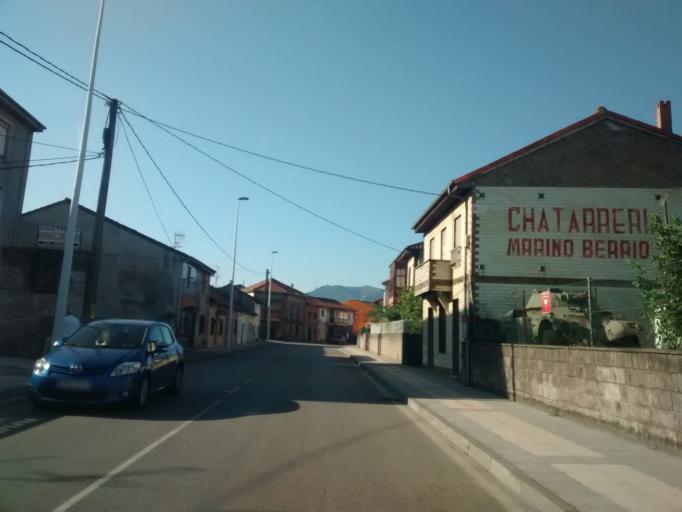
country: ES
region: Cantabria
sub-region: Provincia de Cantabria
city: Torrelavega
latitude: 43.3410
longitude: -4.0585
